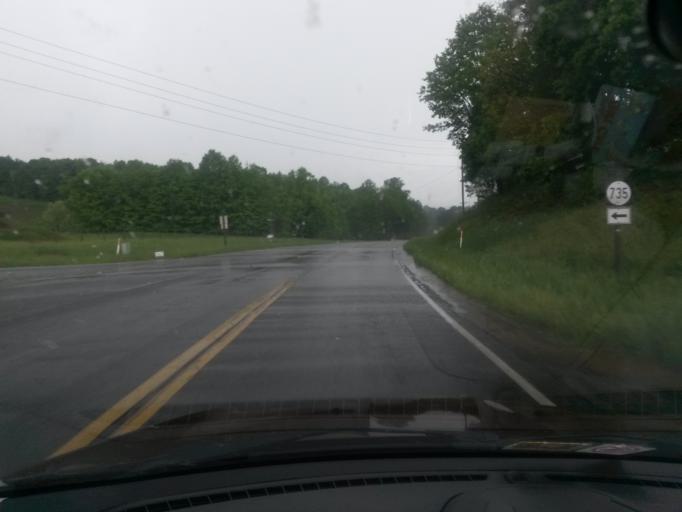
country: US
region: Virginia
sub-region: Floyd County
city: Floyd
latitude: 36.9742
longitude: -80.3991
